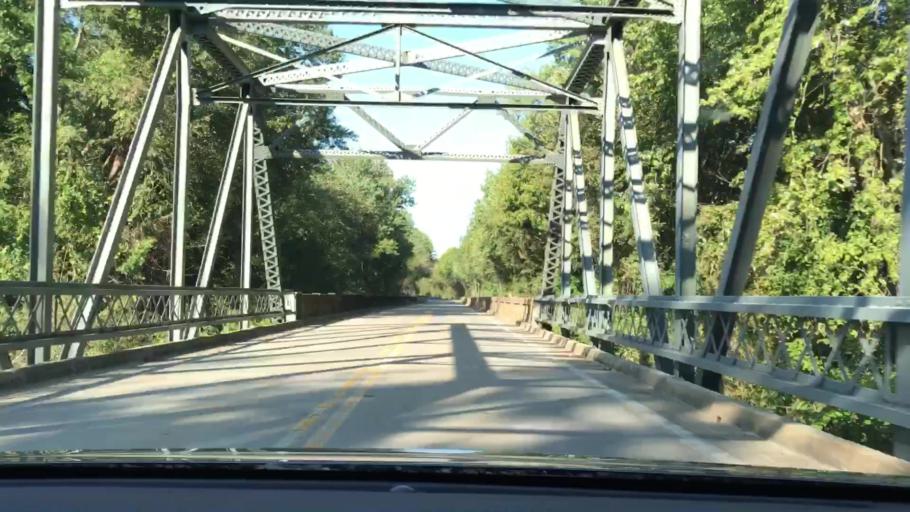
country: US
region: Kentucky
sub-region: Marshall County
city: Benton
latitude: 36.7686
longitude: -88.2778
